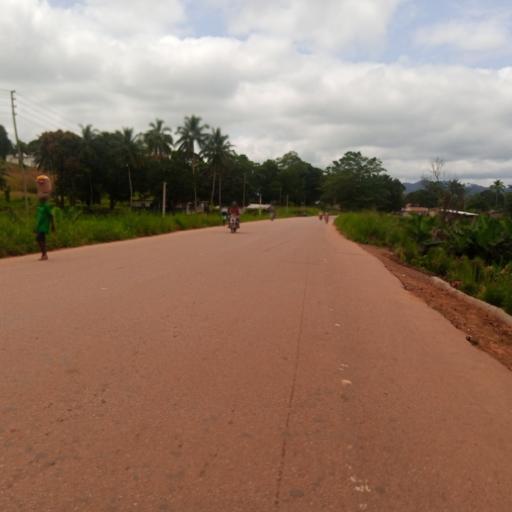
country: SL
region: Eastern Province
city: Kenema
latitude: 7.8618
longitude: -11.1870
